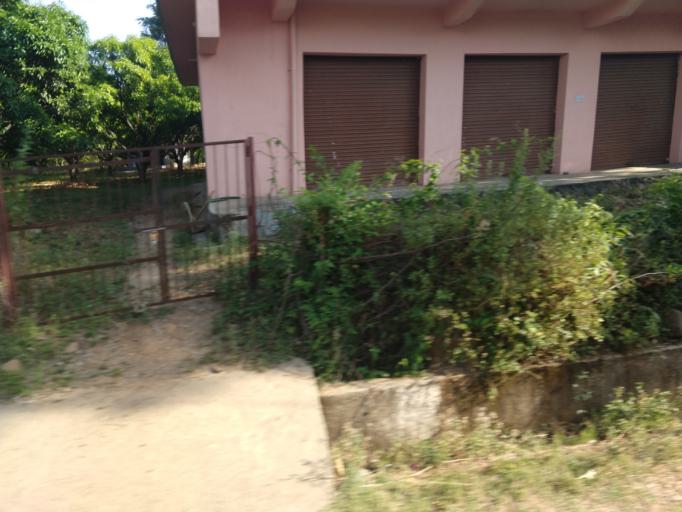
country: IN
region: Himachal Pradesh
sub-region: Chamba
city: Chowari
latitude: 32.3749
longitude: 75.9281
